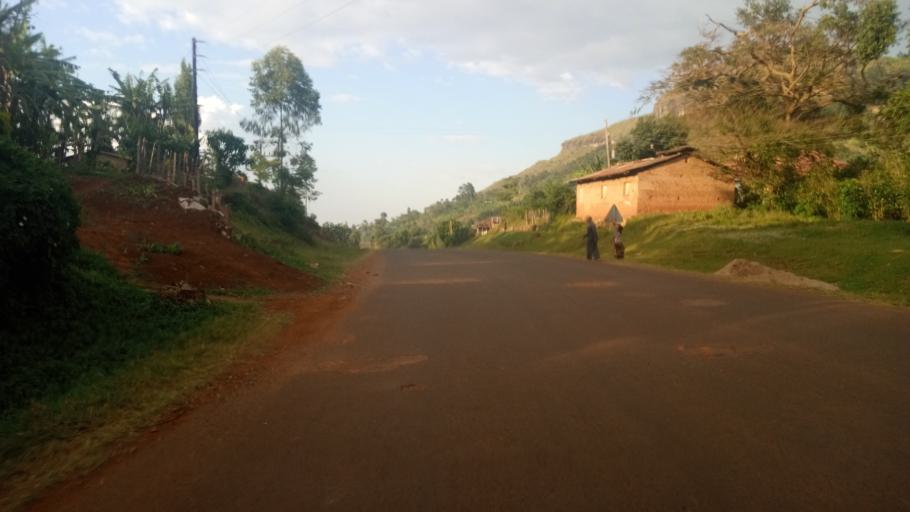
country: UG
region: Eastern Region
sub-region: Kapchorwa District
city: Kapchorwa
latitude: 1.3274
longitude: 34.3564
